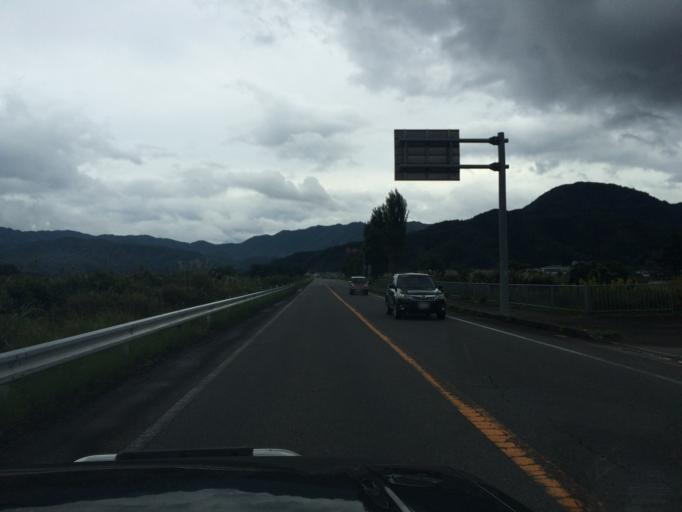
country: JP
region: Hyogo
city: Toyooka
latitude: 35.4468
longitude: 134.7722
